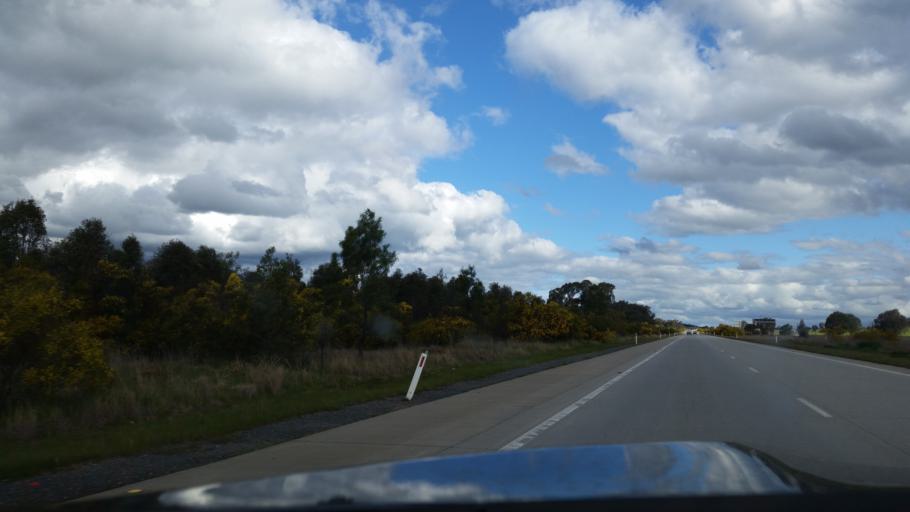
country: AU
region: New South Wales
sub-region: Greater Hume Shire
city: Jindera
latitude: -35.9418
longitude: 147.0035
